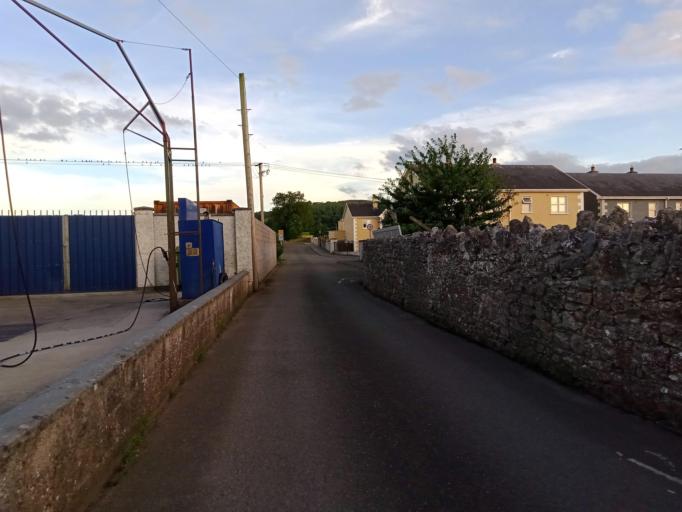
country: IE
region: Leinster
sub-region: Laois
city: Abbeyleix
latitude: 52.8420
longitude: -7.4007
